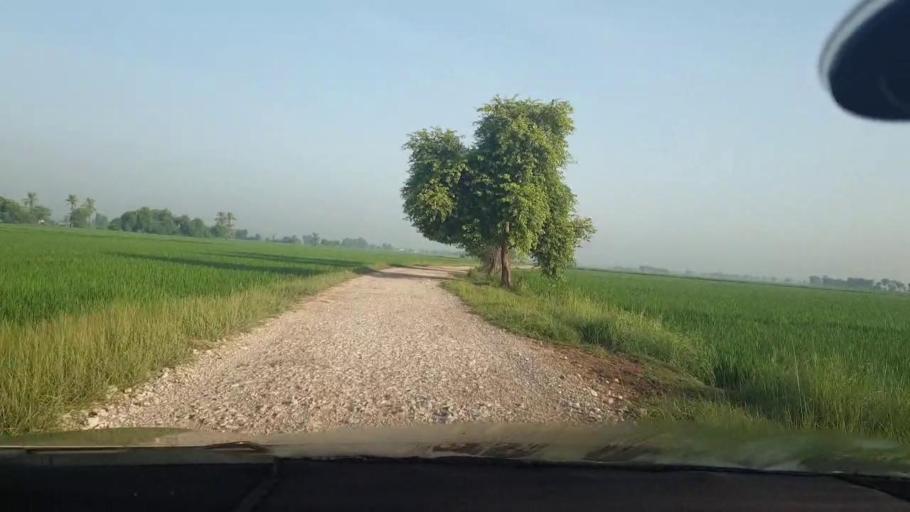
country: PK
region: Sindh
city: Kambar
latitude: 27.6189
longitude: 68.0190
